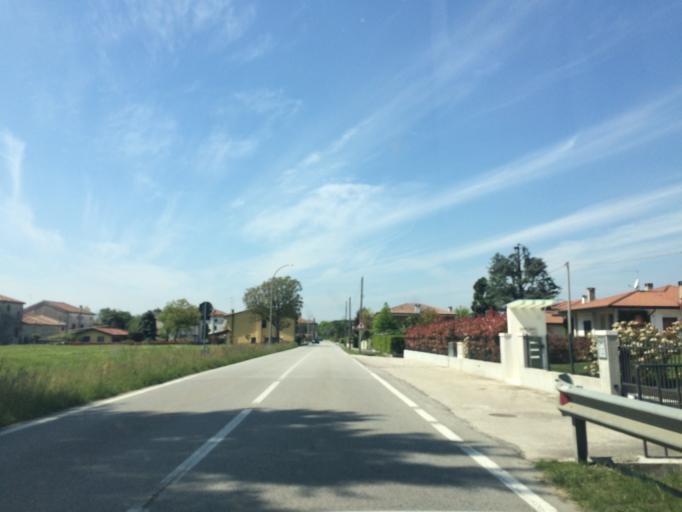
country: IT
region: Veneto
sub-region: Provincia di Padova
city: Fontaniva
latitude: 45.6136
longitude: 11.7762
